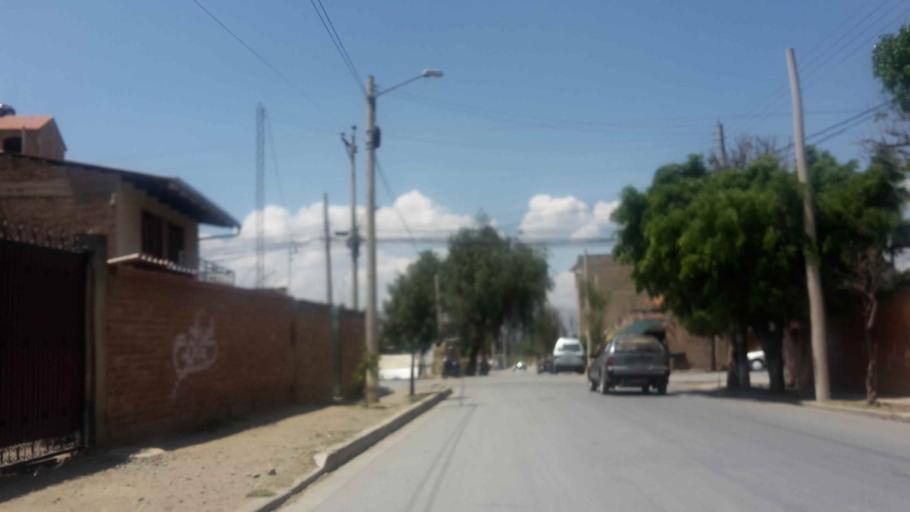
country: BO
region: Cochabamba
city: Cochabamba
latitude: -17.3402
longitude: -66.2154
